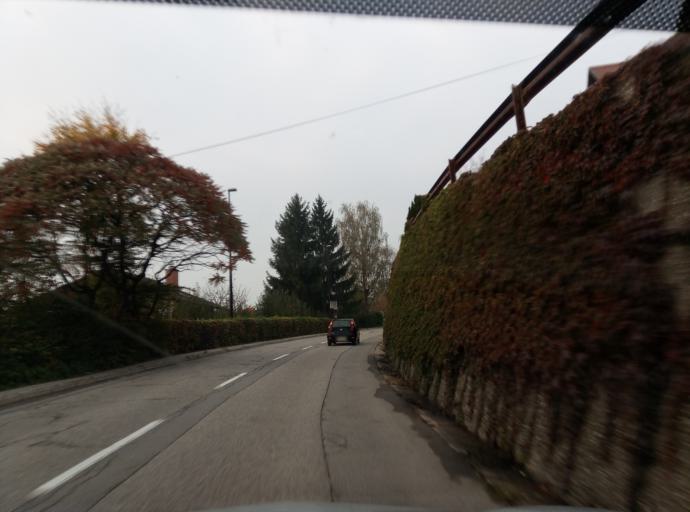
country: SI
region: Ljubljana
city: Ljubljana
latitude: 46.0888
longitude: 14.4675
